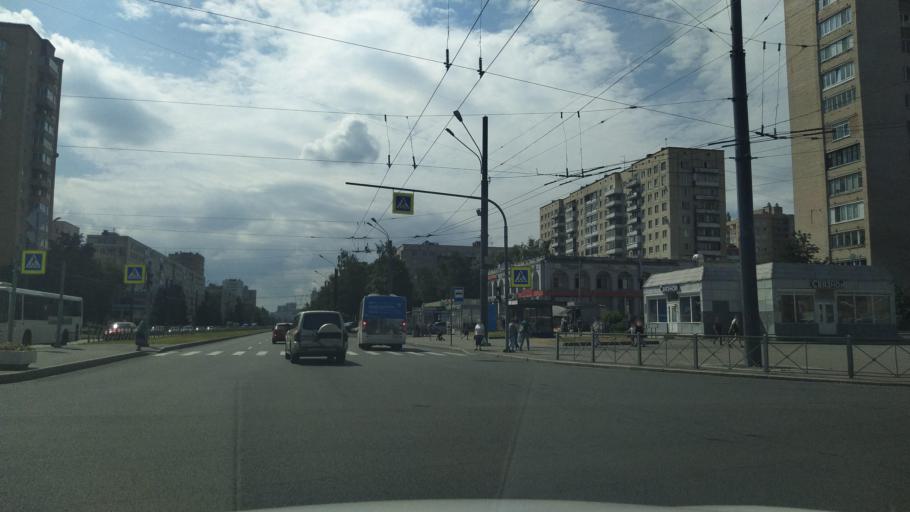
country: RU
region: Leningrad
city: Parnas
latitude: 60.0489
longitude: 30.3540
